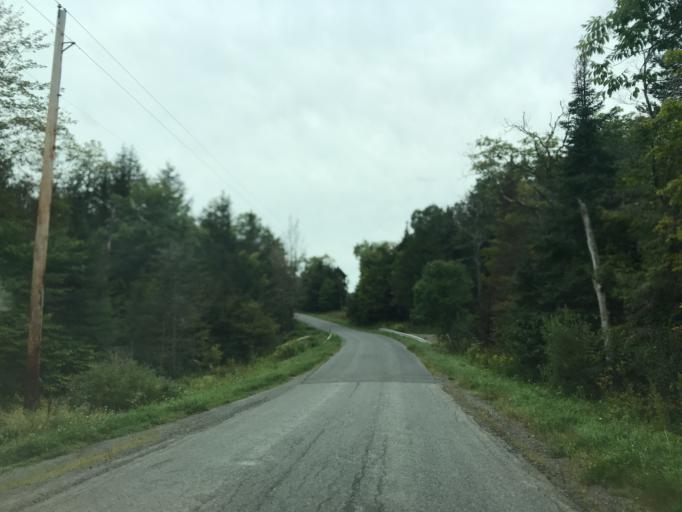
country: US
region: New York
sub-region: Delaware County
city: Stamford
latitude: 42.5143
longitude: -74.6419
